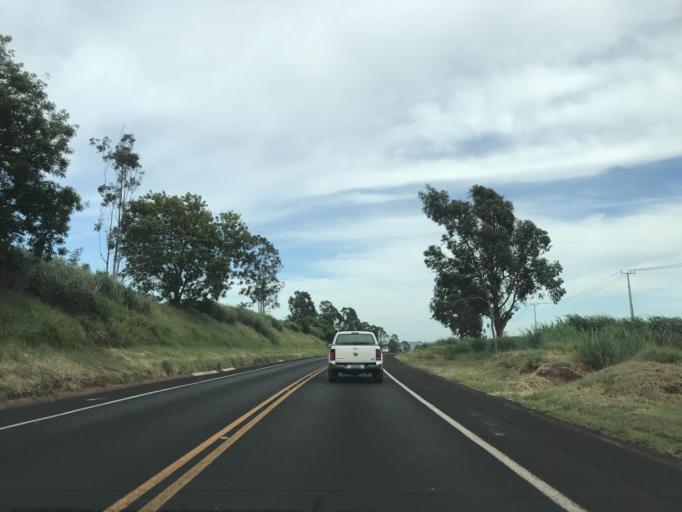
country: BR
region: Parana
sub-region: Paranavai
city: Paranavai
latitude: -23.0143
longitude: -52.5328
